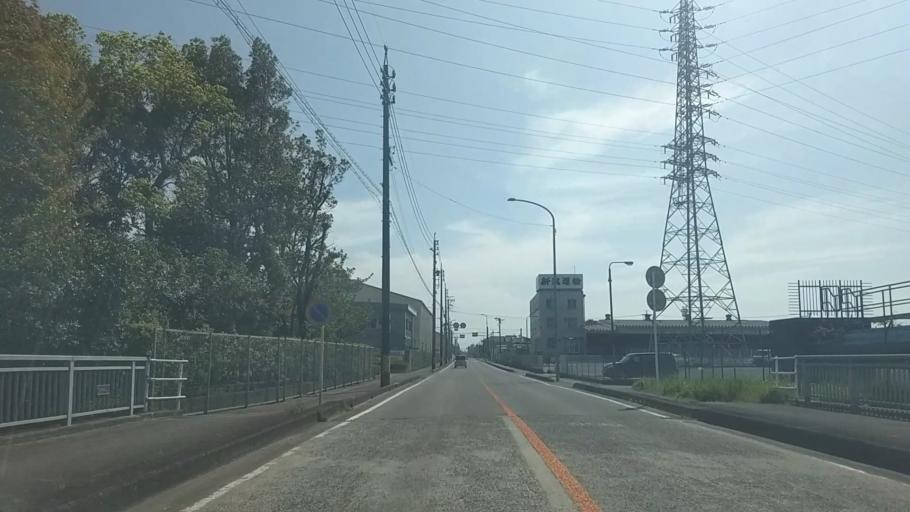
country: JP
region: Aichi
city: Anjo
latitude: 34.9730
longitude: 137.1090
